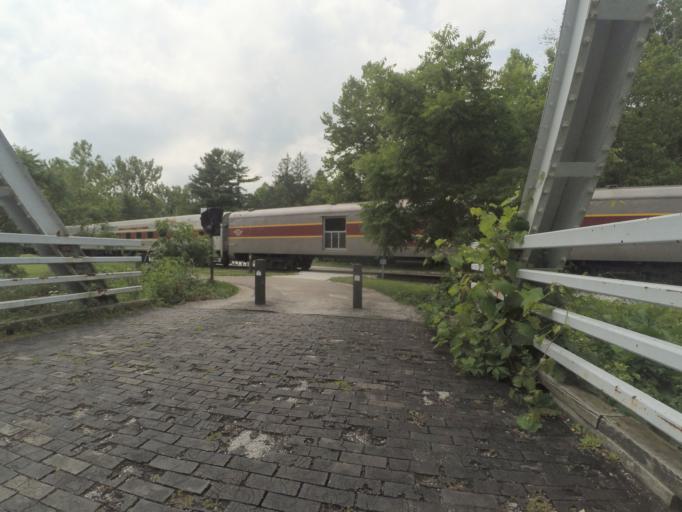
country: US
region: Ohio
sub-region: Cuyahoga County
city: Brecksville
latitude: 41.3193
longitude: -81.5877
